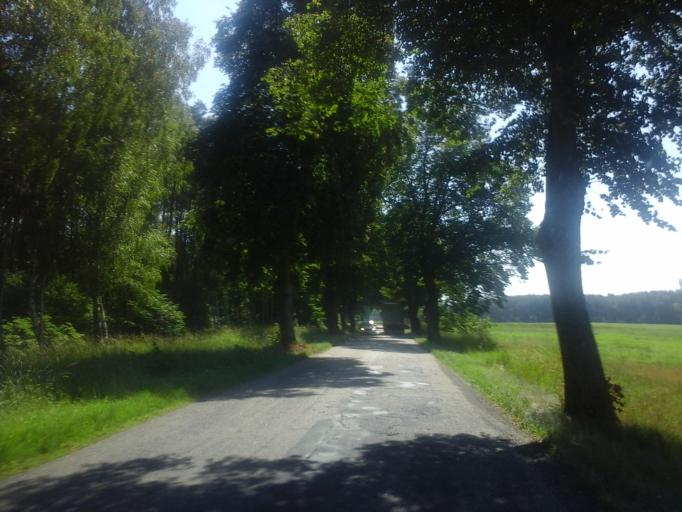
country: PL
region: West Pomeranian Voivodeship
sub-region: Powiat bialogardzki
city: Tychowo
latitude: 54.0297
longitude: 16.1694
